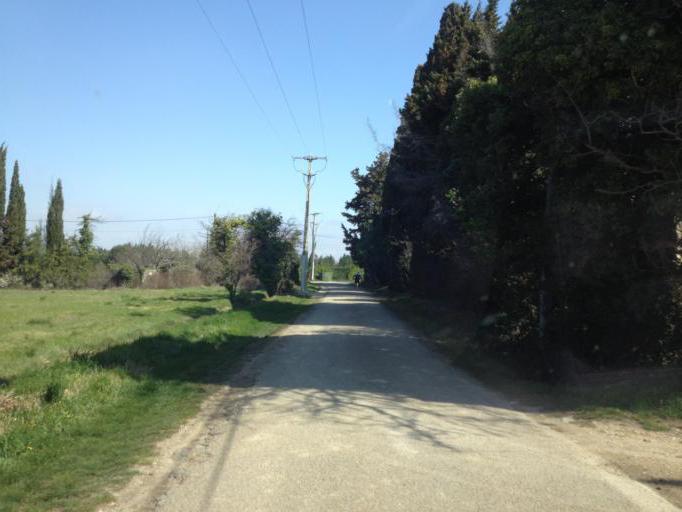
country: FR
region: Provence-Alpes-Cote d'Azur
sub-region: Departement du Vaucluse
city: Jonquieres
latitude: 44.1367
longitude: 4.9238
